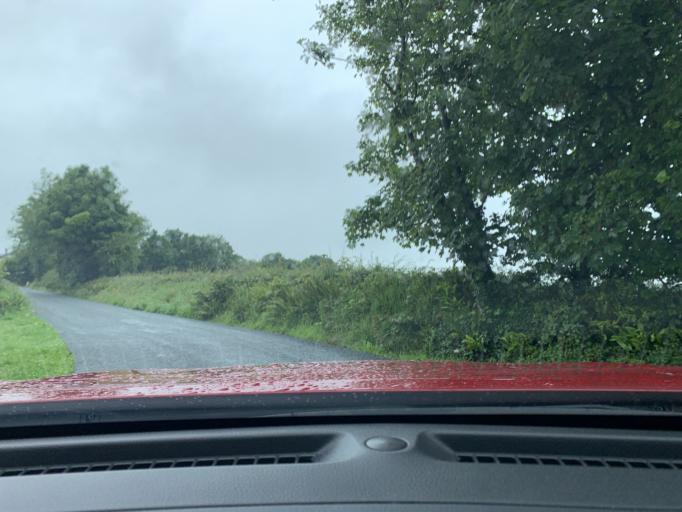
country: IE
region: Connaught
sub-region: Sligo
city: Sligo
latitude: 54.3071
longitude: -8.4612
